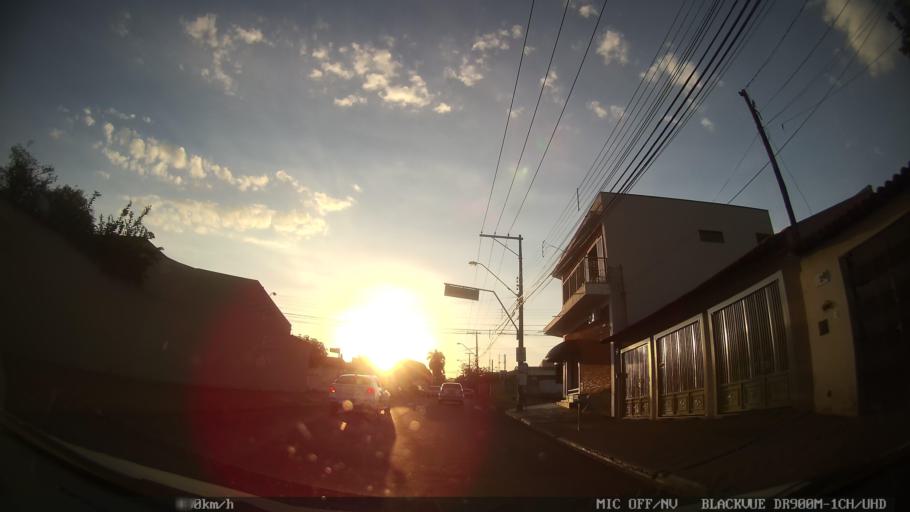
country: BR
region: Sao Paulo
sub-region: Ribeirao Preto
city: Ribeirao Preto
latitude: -21.1614
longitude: -47.8326
